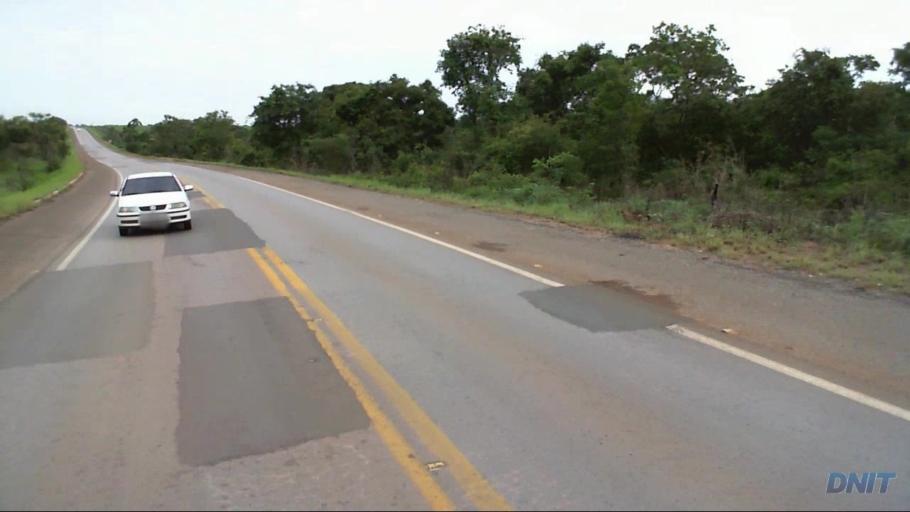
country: BR
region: Goias
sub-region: Uruacu
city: Uruacu
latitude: -14.7268
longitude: -49.0949
